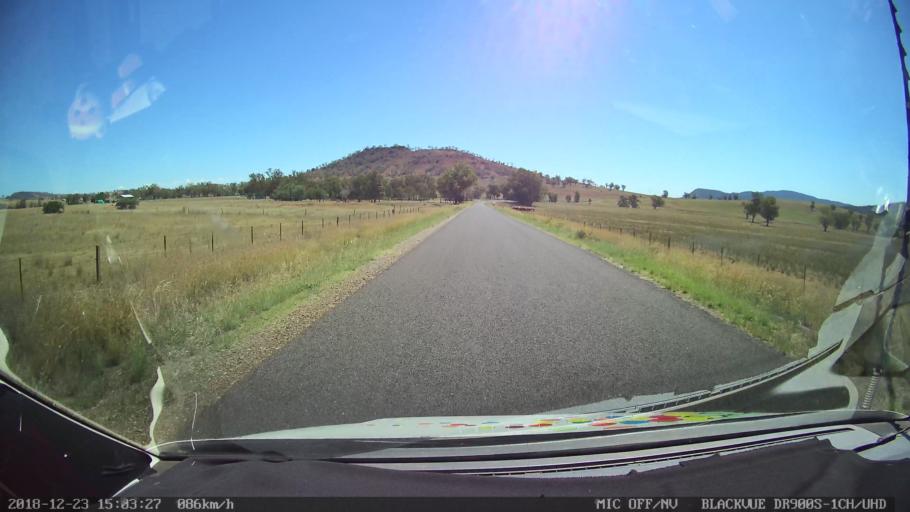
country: AU
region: New South Wales
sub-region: Tamworth Municipality
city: Manilla
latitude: -30.7386
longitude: 150.7649
